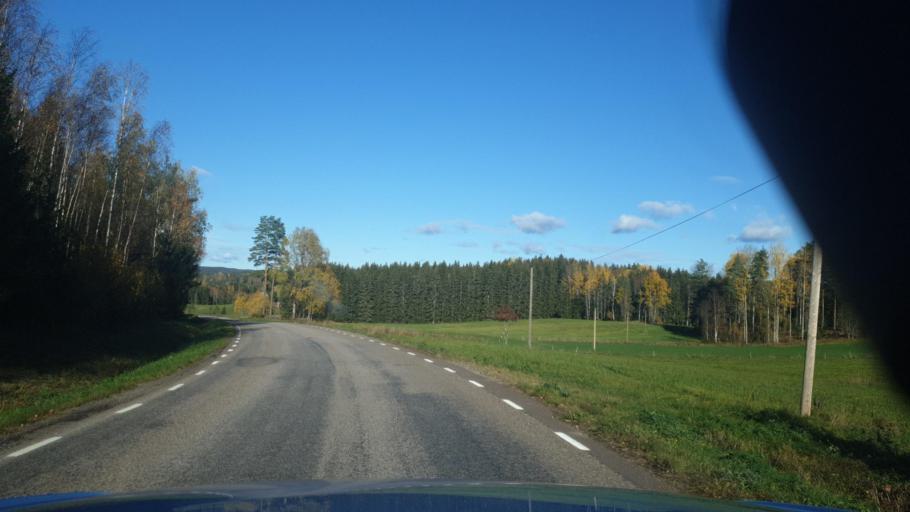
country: SE
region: Vaermland
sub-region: Arvika Kommun
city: Arvika
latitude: 59.6230
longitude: 12.7954
